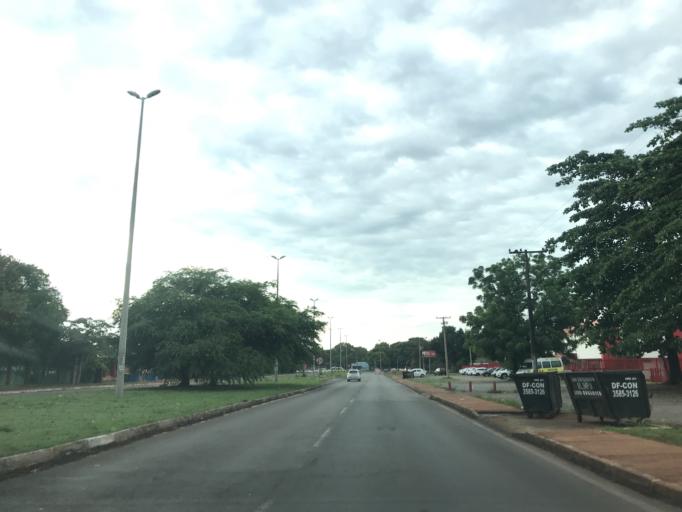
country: BR
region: Federal District
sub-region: Brasilia
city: Brasilia
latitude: -15.8150
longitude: -47.9216
